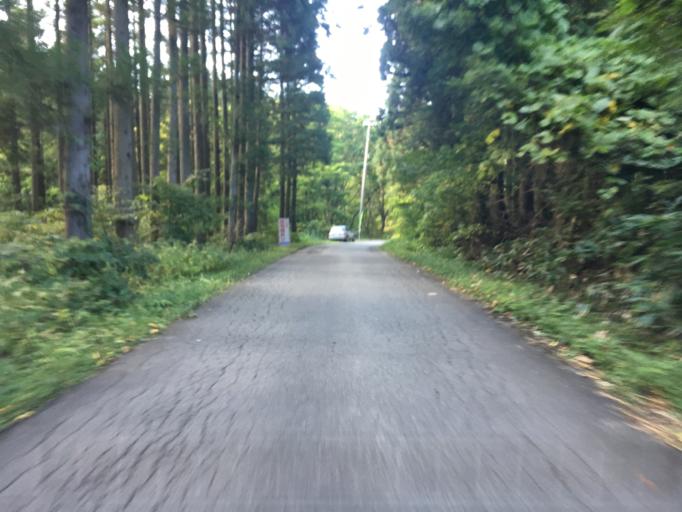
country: JP
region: Yamagata
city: Yonezawa
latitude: 37.8491
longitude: 140.1771
